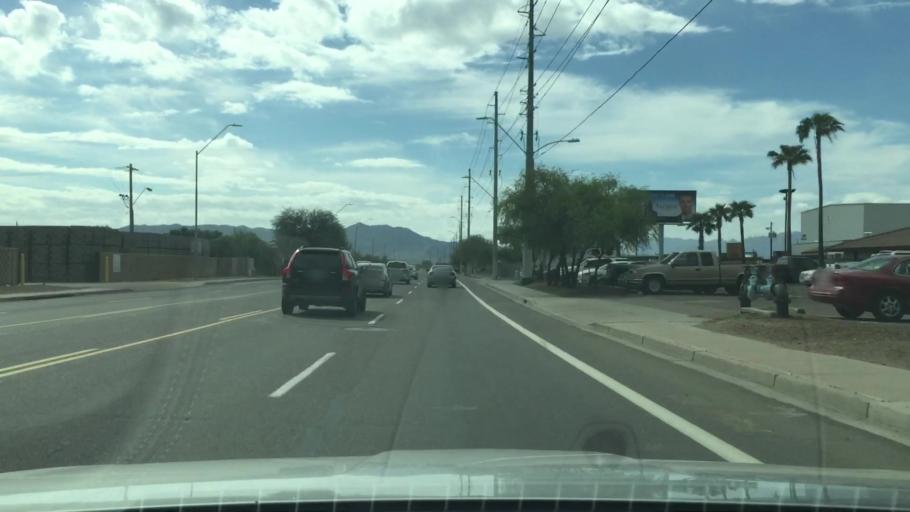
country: US
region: Arizona
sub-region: Maricopa County
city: Phoenix
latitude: 33.4214
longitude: -112.1346
